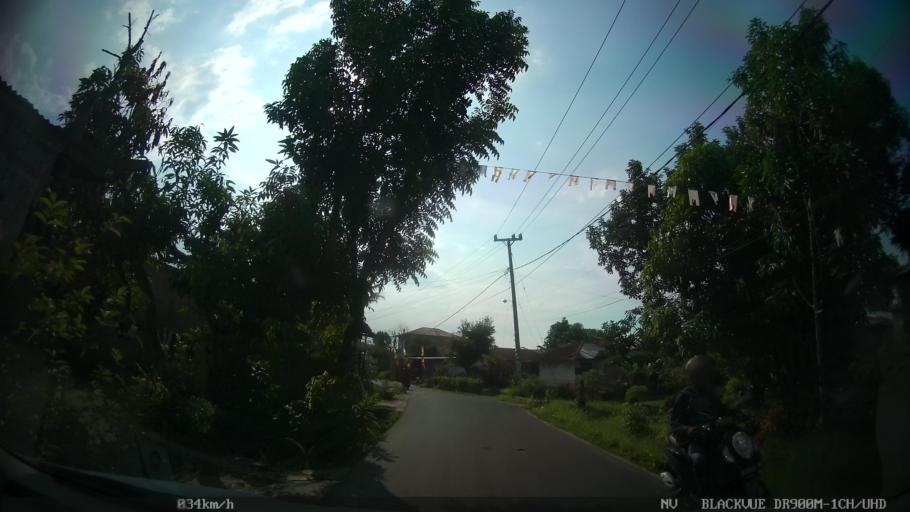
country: ID
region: North Sumatra
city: Medan
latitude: 3.5941
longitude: 98.7644
